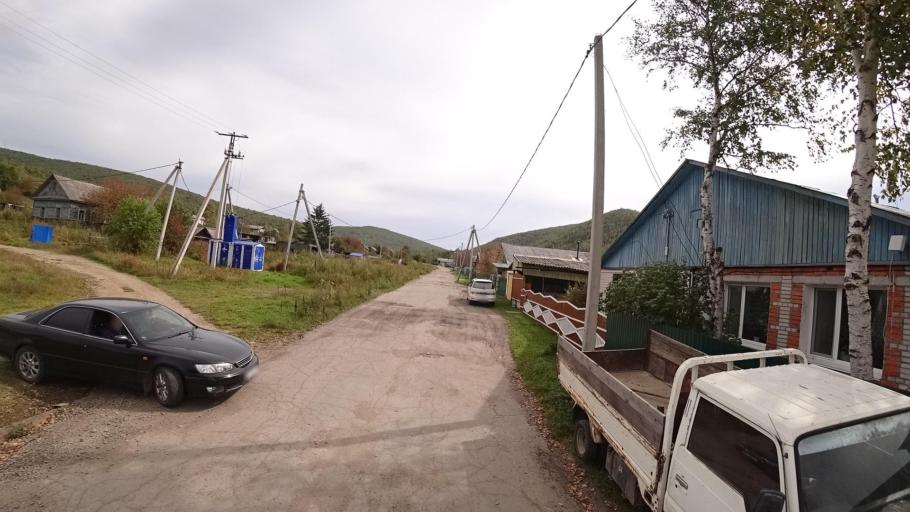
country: RU
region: Jewish Autonomous Oblast
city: Khingansk
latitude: 49.1238
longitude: 131.2038
